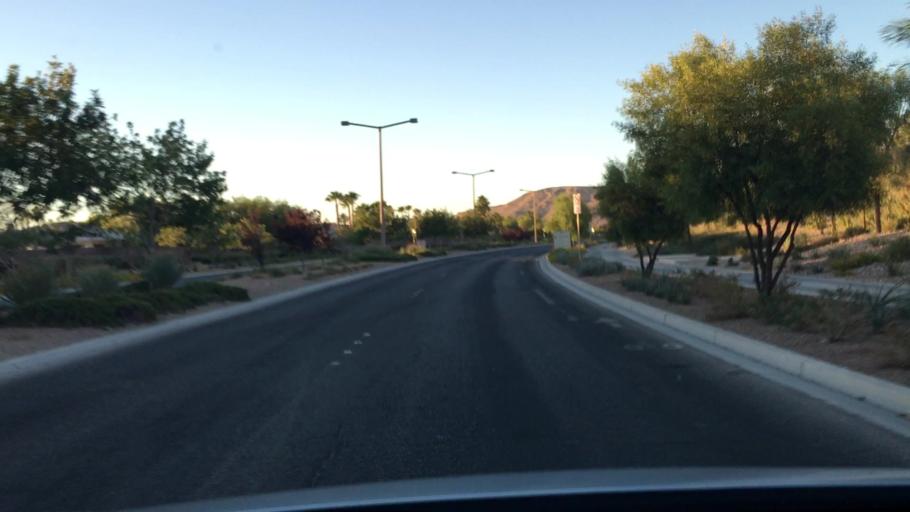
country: US
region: Nevada
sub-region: Clark County
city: Summerlin South
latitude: 36.1071
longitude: -115.3275
